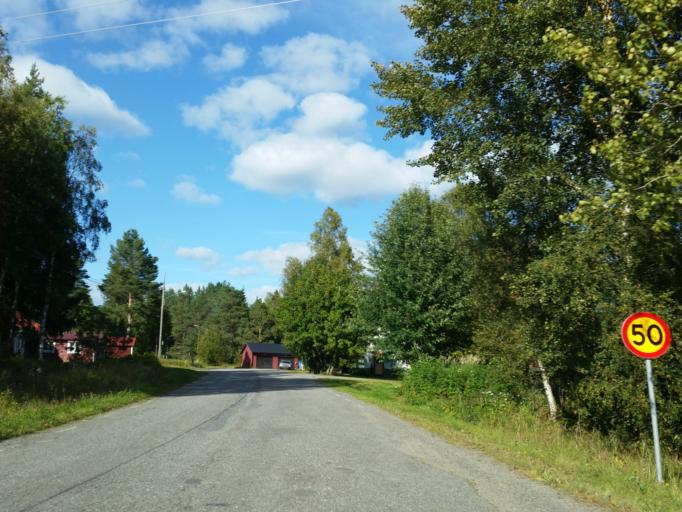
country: SE
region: Vaesterbotten
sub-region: Robertsfors Kommun
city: Robertsfors
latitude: 64.0522
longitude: 20.8545
